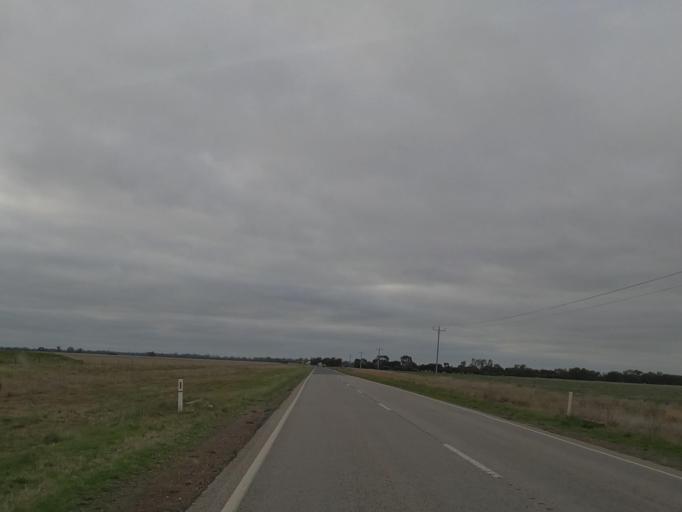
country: AU
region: Victoria
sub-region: Greater Bendigo
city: Long Gully
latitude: -36.4699
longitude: 143.9636
